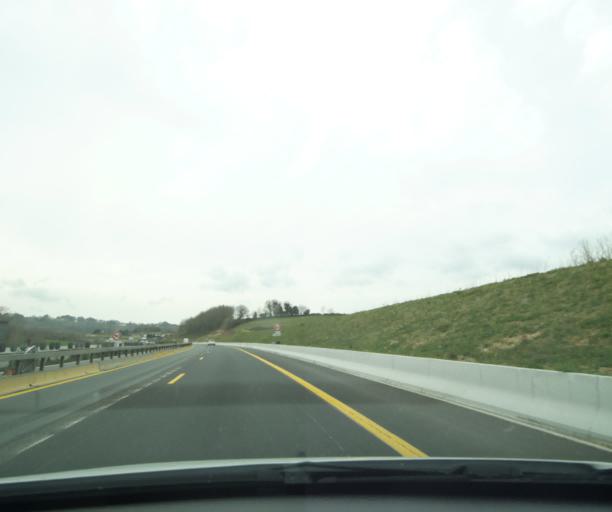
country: FR
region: Aquitaine
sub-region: Departement des Pyrenees-Atlantiques
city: Urrugne
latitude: 43.3586
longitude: -1.7083
